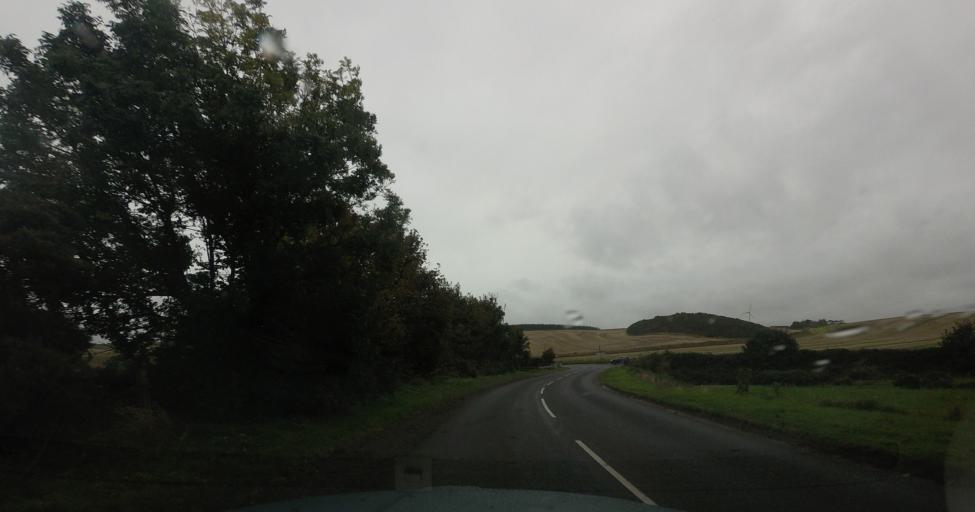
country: GB
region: Scotland
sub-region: Aberdeenshire
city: Whitehills
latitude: 57.6655
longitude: -2.5639
